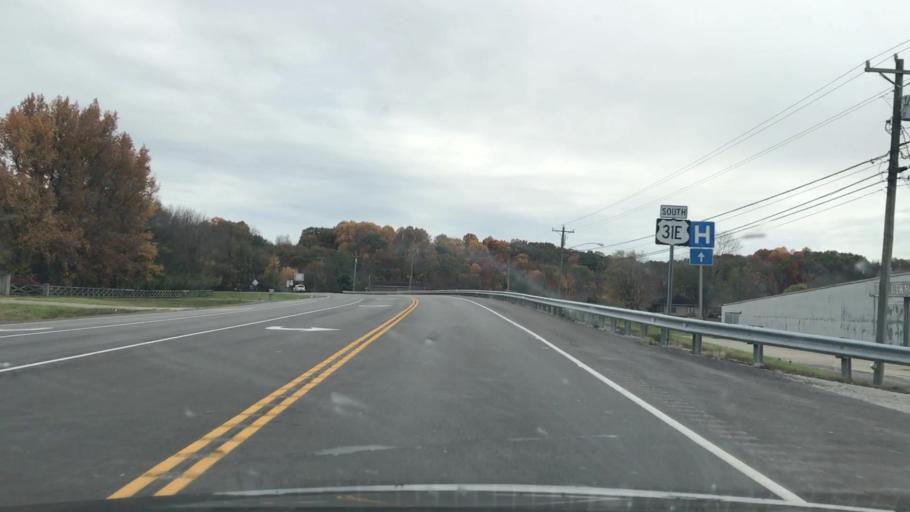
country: US
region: Kentucky
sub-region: Barren County
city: Glasgow
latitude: 37.0323
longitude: -85.9065
